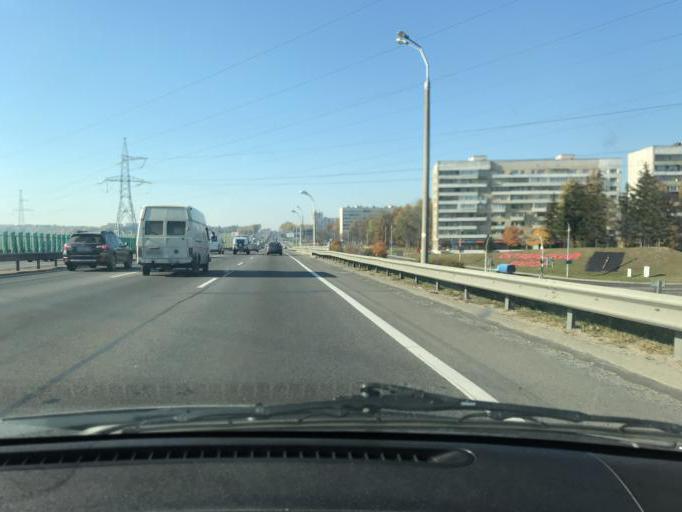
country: BY
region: Minsk
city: Yubilyeyny
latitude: 53.8387
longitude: 27.5042
